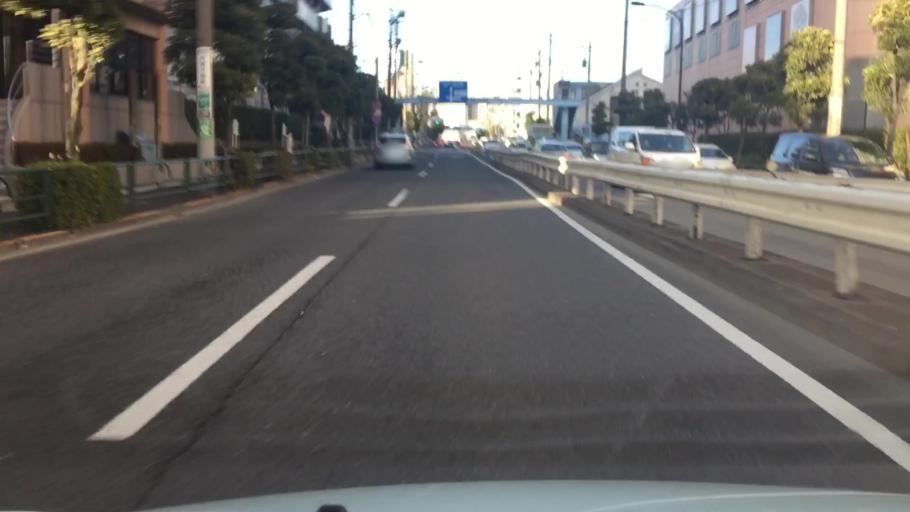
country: JP
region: Saitama
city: Soka
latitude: 35.7743
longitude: 139.7846
